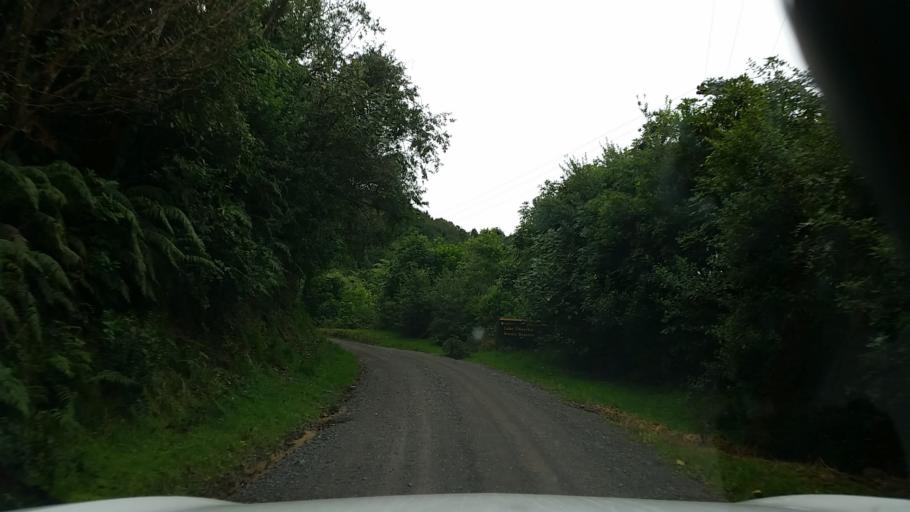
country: NZ
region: Bay of Plenty
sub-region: Rotorua District
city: Rotorua
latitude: -38.1592
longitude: 176.3615
